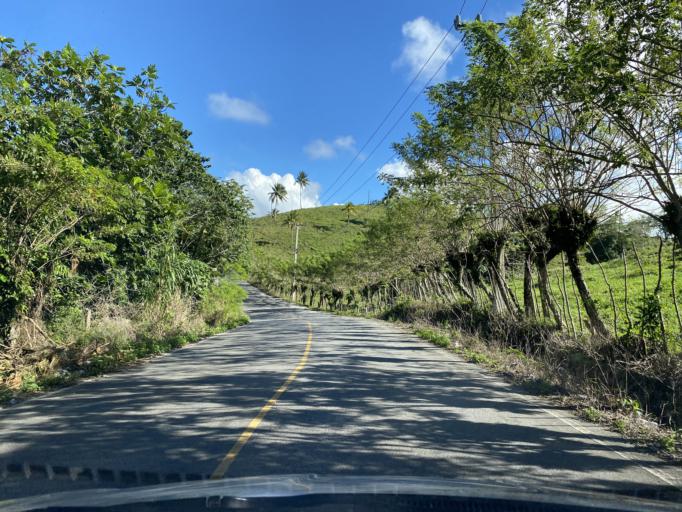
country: DO
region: Samana
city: Sanchez
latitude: 19.2508
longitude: -69.5914
